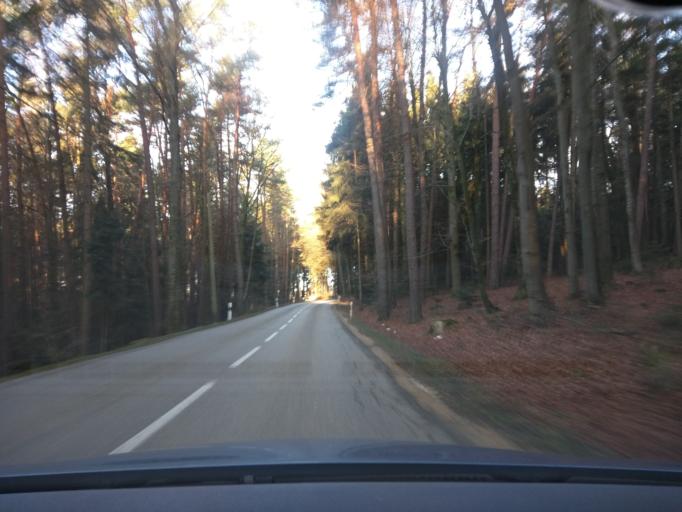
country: DE
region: Bavaria
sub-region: Upper Bavaria
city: Wolnzach
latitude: 48.5855
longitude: 11.6535
